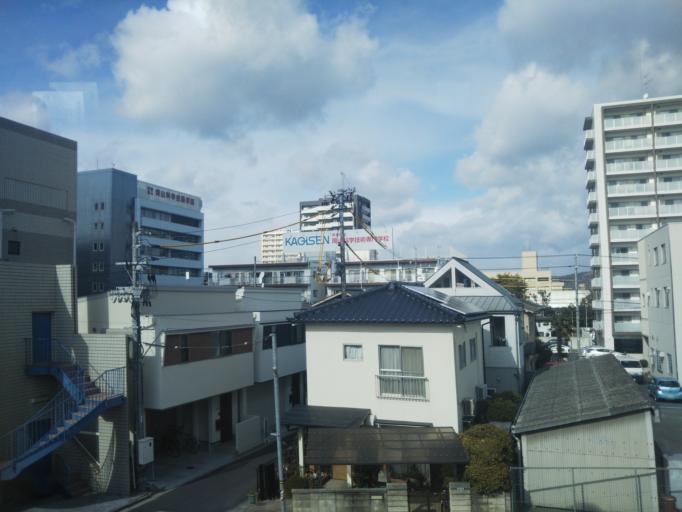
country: JP
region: Okayama
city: Okayama-shi
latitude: 34.6624
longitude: 133.9128
